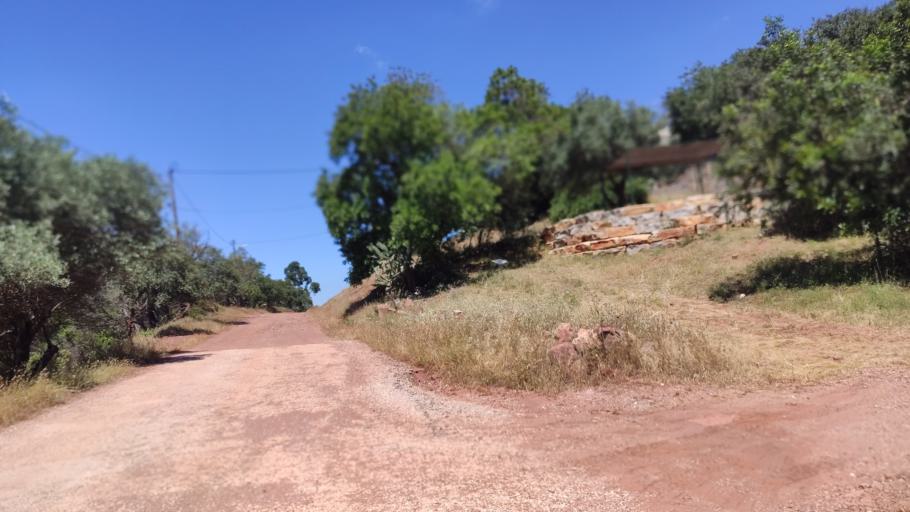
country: PT
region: Faro
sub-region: Sao Bras de Alportel
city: Sao Bras de Alportel
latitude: 37.1744
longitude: -7.9276
